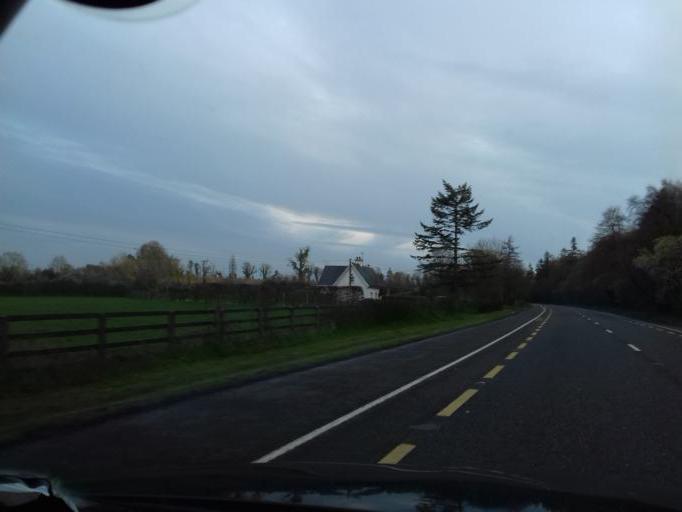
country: IE
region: Leinster
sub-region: Laois
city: Abbeyleix
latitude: 52.8718
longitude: -7.3631
